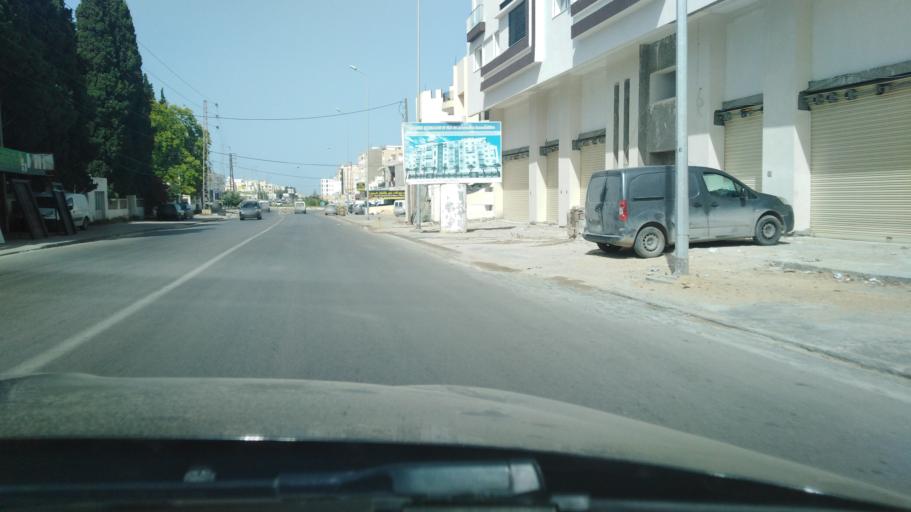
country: TN
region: Susah
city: Sousse
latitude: 35.8078
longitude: 10.6210
